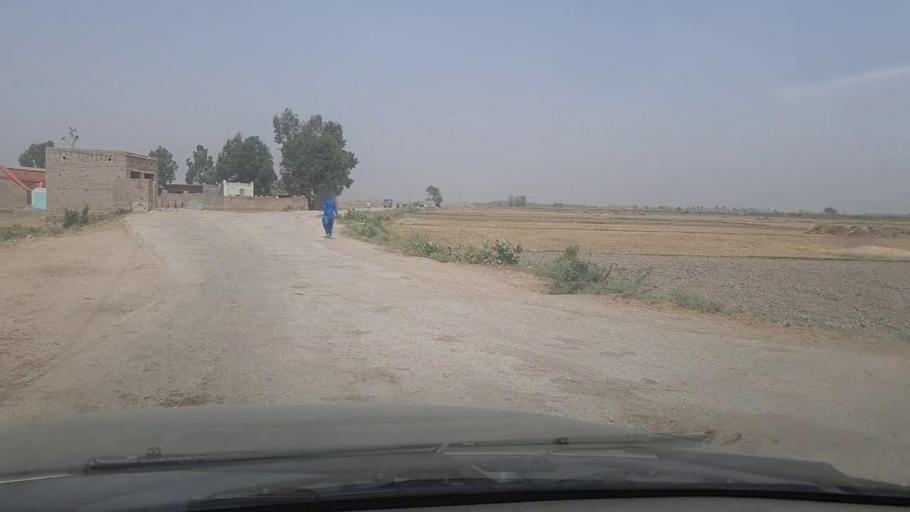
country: PK
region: Sindh
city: Madeji
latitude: 27.8041
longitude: 68.4014
